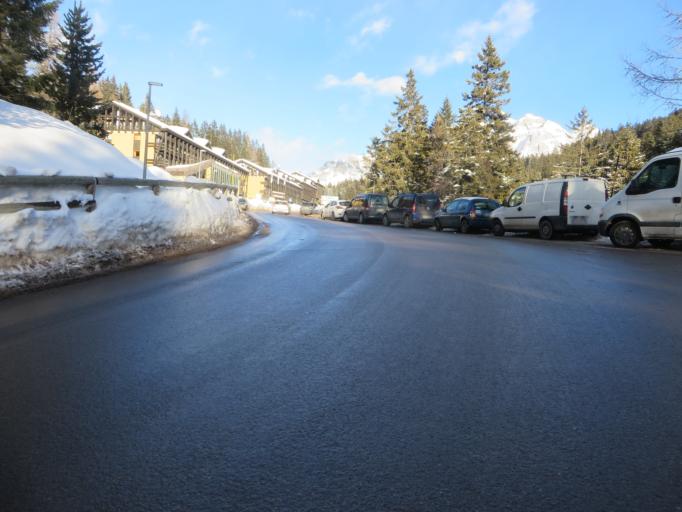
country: IT
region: Trentino-Alto Adige
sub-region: Provincia di Trento
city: Commezzadura
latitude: 46.2346
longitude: 10.8324
